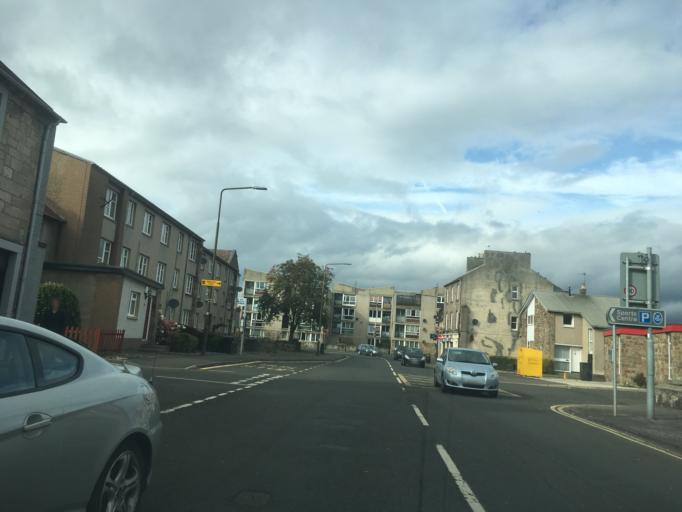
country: GB
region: Scotland
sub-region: East Lothian
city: Musselburgh
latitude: 55.9394
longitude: -3.0479
